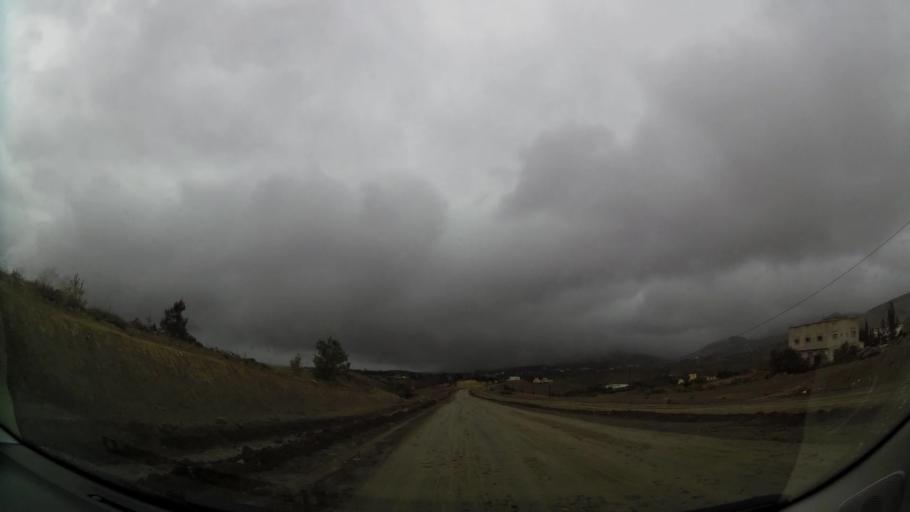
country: MA
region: Oriental
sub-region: Nador
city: Midar
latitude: 34.8953
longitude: -3.7686
